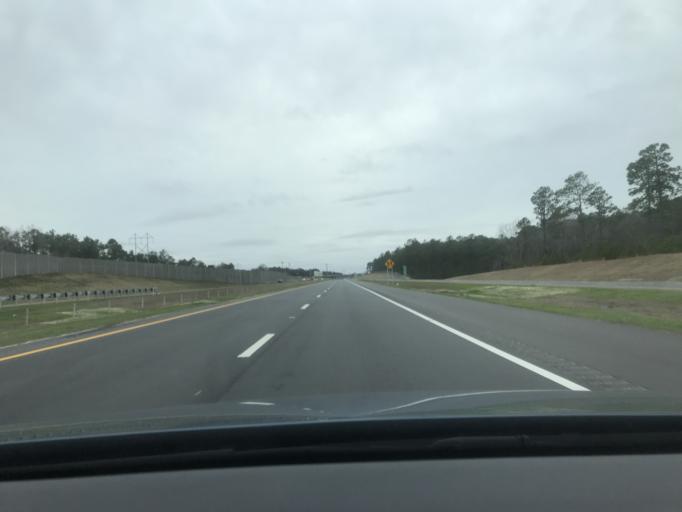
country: US
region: North Carolina
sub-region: Cumberland County
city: Fort Bragg
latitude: 35.1096
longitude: -78.9854
